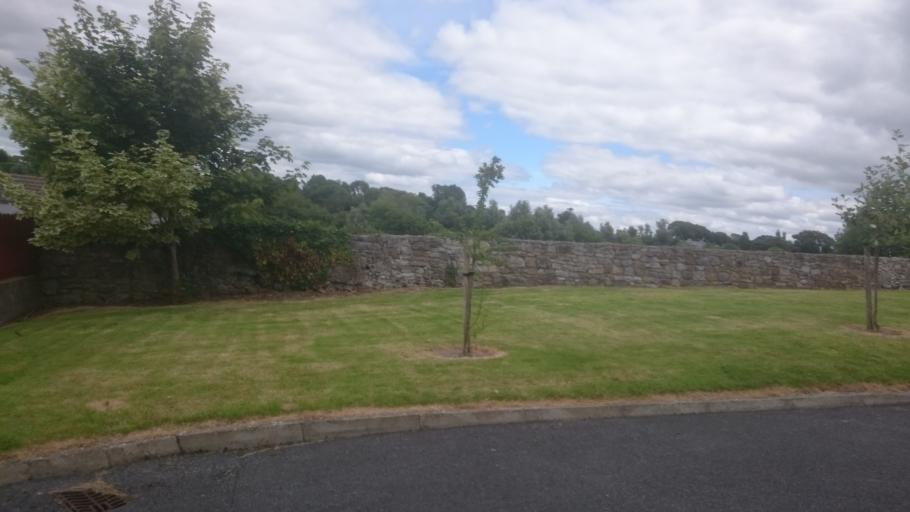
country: IE
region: Leinster
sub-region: Kilkenny
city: Kilkenny
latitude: 52.5399
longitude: -7.2725
